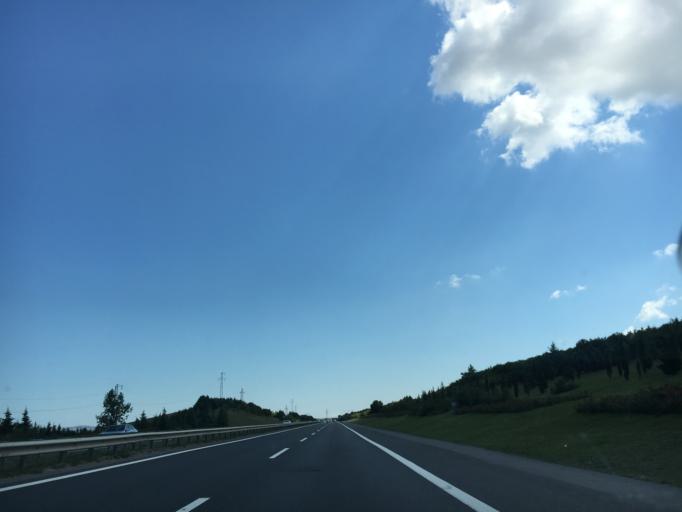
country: TR
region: Istanbul
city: Canta
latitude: 41.0813
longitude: 28.1304
